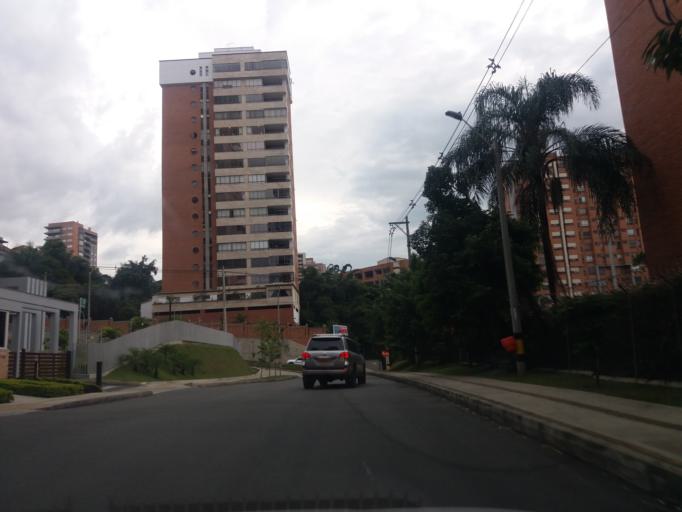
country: CO
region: Antioquia
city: Itagui
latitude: 6.2030
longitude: -75.5691
